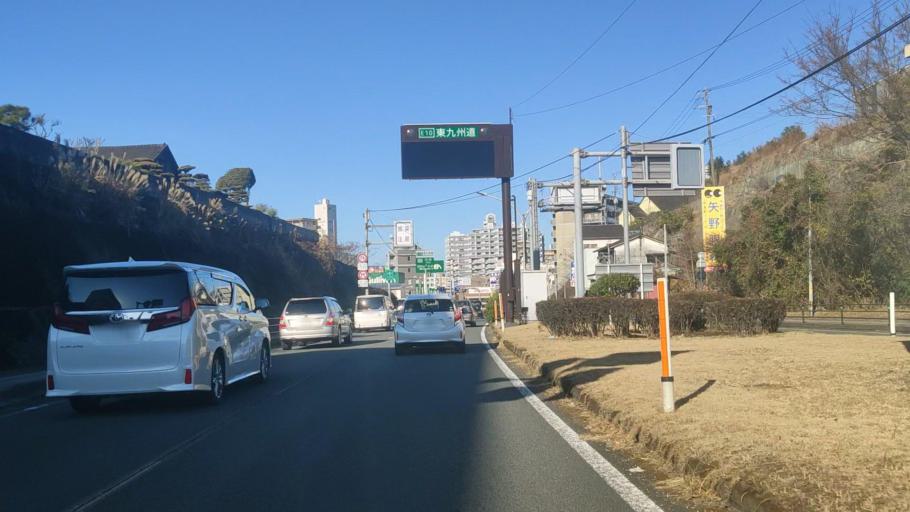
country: JP
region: Oita
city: Oita
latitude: 33.2229
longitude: 131.5951
